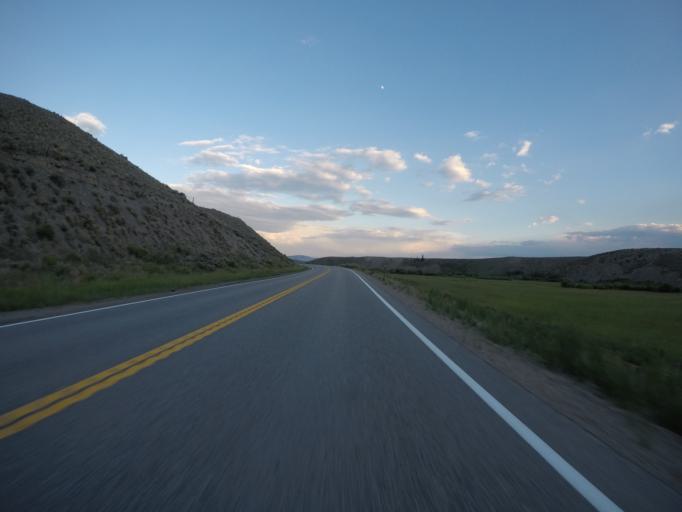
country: US
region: Colorado
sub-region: Grand County
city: Kremmling
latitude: 40.2487
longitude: -106.4506
